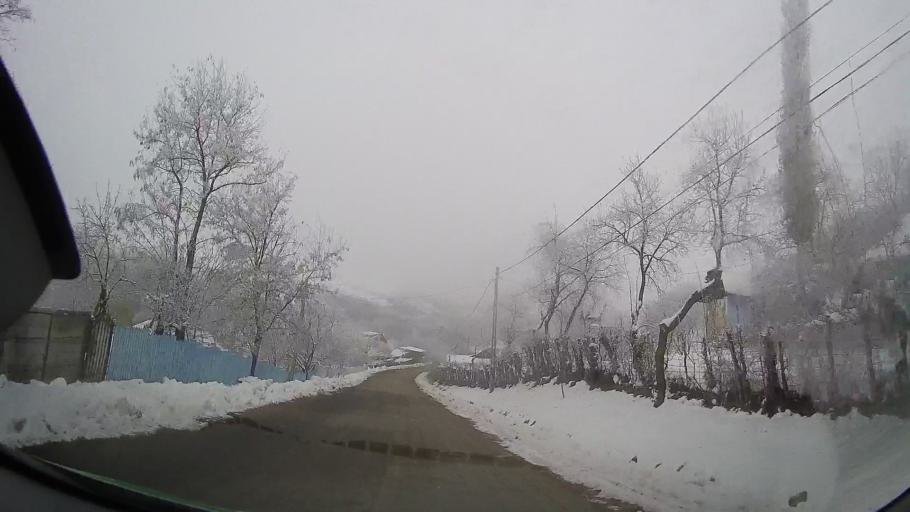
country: RO
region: Iasi
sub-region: Comuna Tansa
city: Suhulet
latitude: 46.8947
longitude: 27.2822
